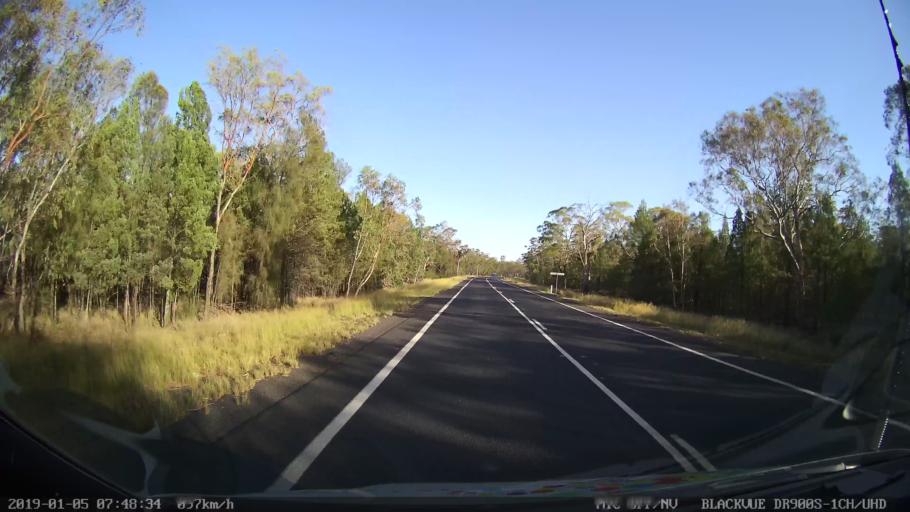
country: AU
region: New South Wales
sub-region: Gilgandra
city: Gilgandra
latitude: -31.8144
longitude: 148.6375
